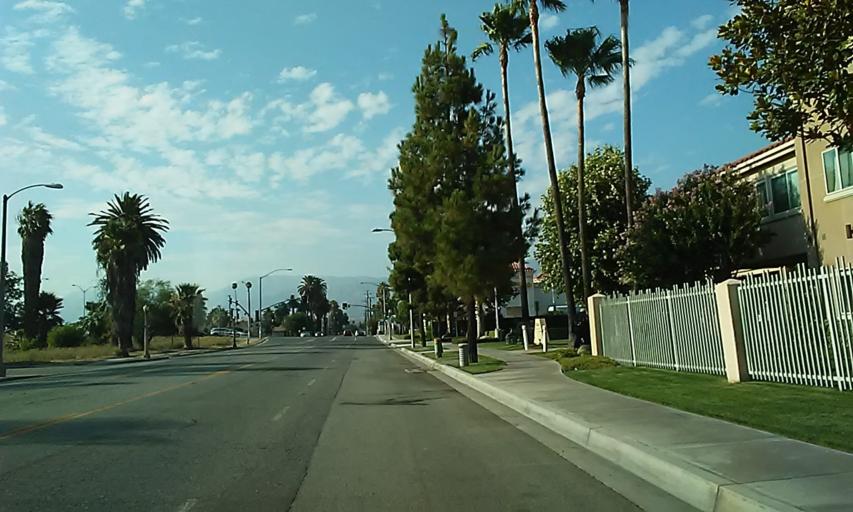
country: US
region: California
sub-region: San Bernardino County
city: San Bernardino
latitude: 34.1070
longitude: -117.3008
